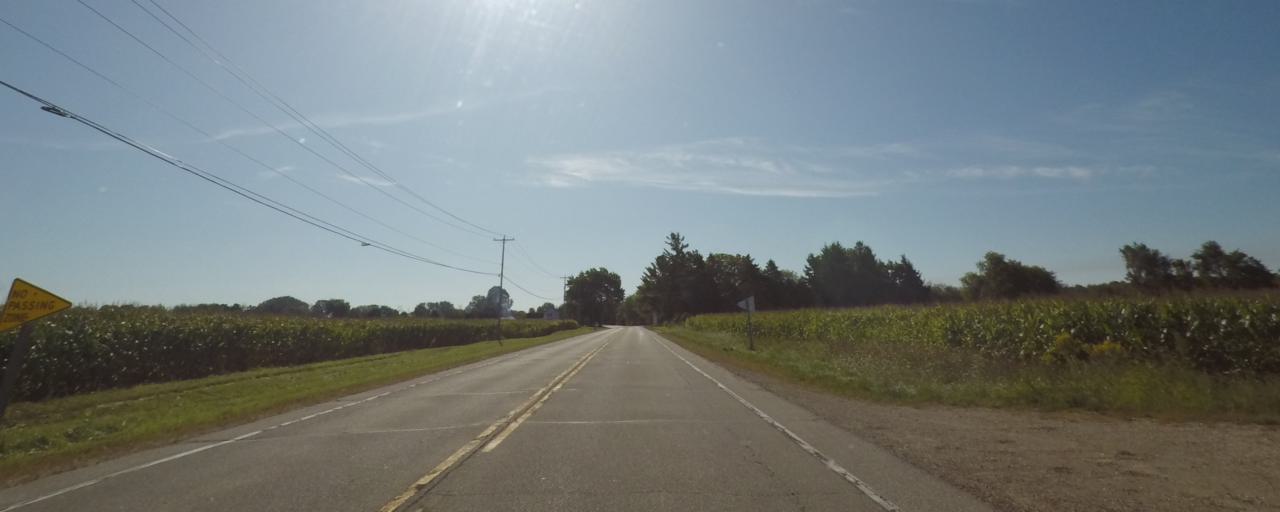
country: US
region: Wisconsin
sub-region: Waukesha County
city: Dousman
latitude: 43.0249
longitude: -88.5034
